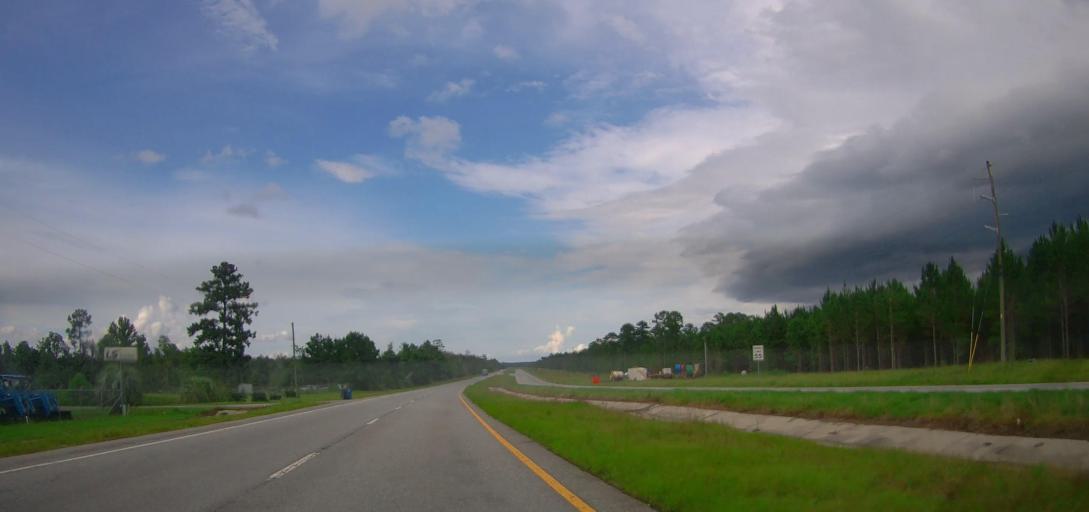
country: US
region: Georgia
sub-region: Pierce County
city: Blackshear
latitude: 31.4334
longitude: -82.0887
